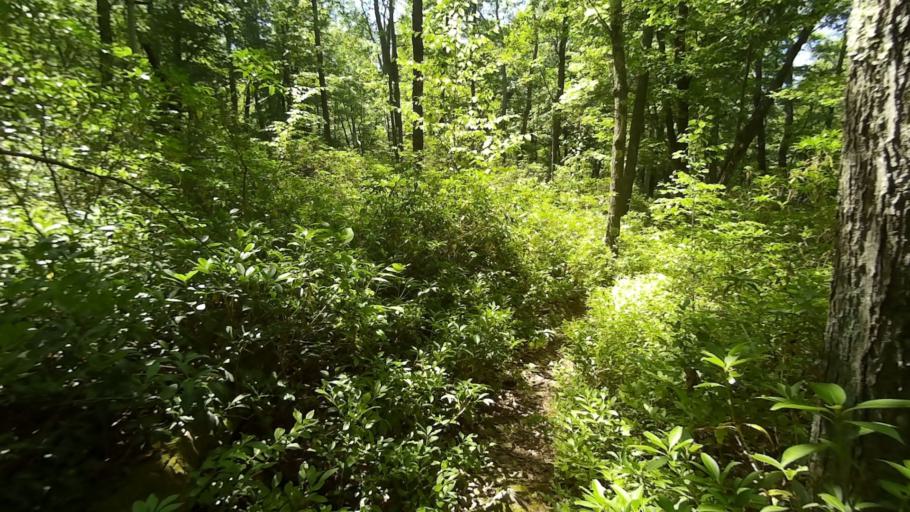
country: US
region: Pennsylvania
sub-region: Centre County
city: Boalsburg
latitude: 40.7204
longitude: -77.7763
